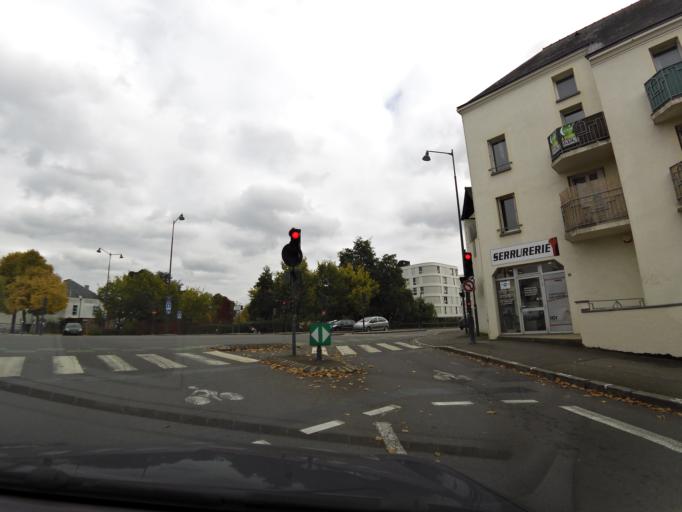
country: FR
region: Brittany
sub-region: Departement d'Ille-et-Vilaine
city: Rennes
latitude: 48.1205
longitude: -1.6822
